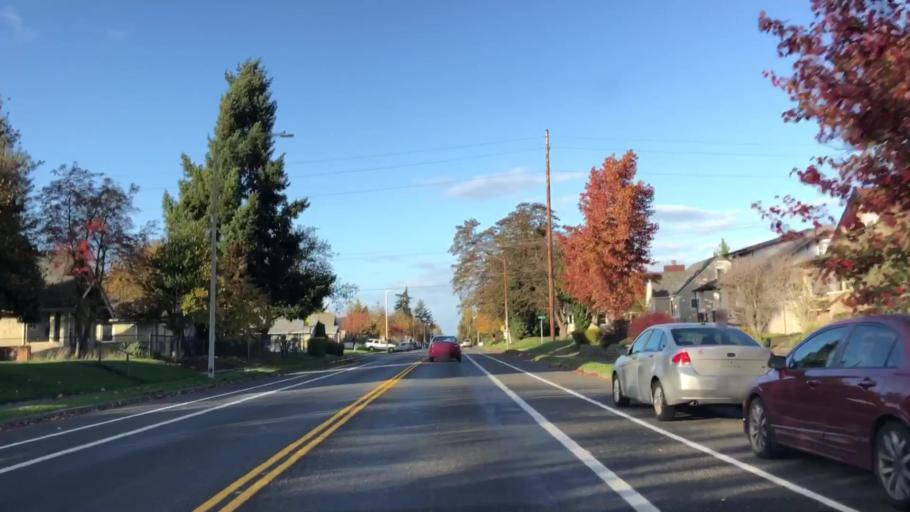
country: US
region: Washington
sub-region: Pierce County
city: Parkland
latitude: 47.2010
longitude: -122.4432
